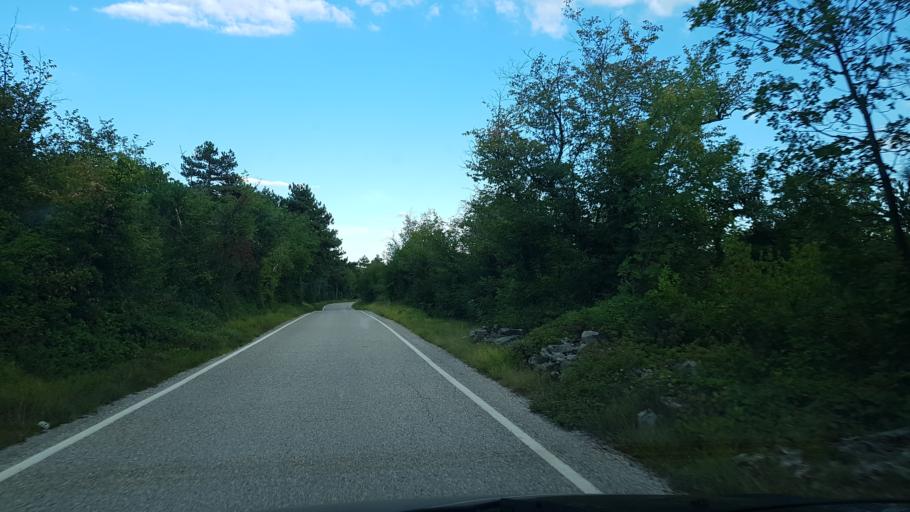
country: SI
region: Rence-Vogrsko
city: Rence
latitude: 45.8537
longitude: 13.6736
